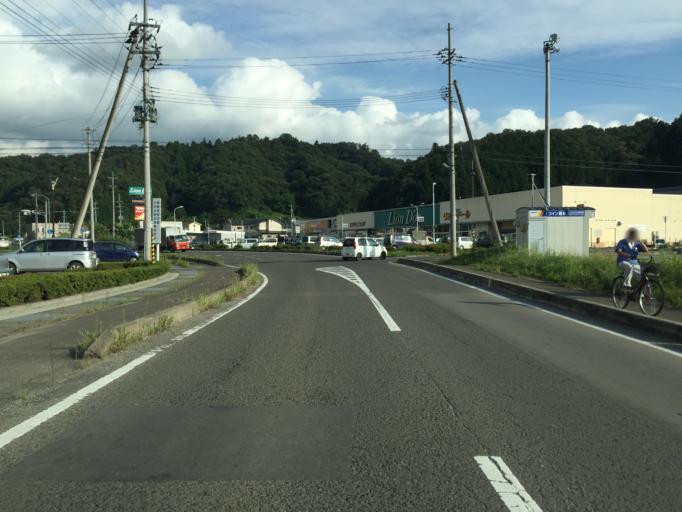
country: JP
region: Fukushima
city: Fukushima-shi
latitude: 37.6661
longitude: 140.5767
